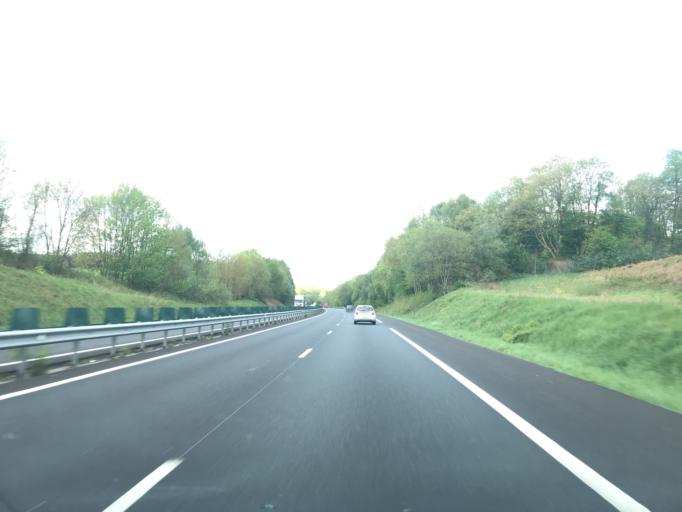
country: FR
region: Haute-Normandie
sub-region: Departement de l'Eure
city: Pont-Audemer
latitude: 49.3921
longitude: 0.5173
